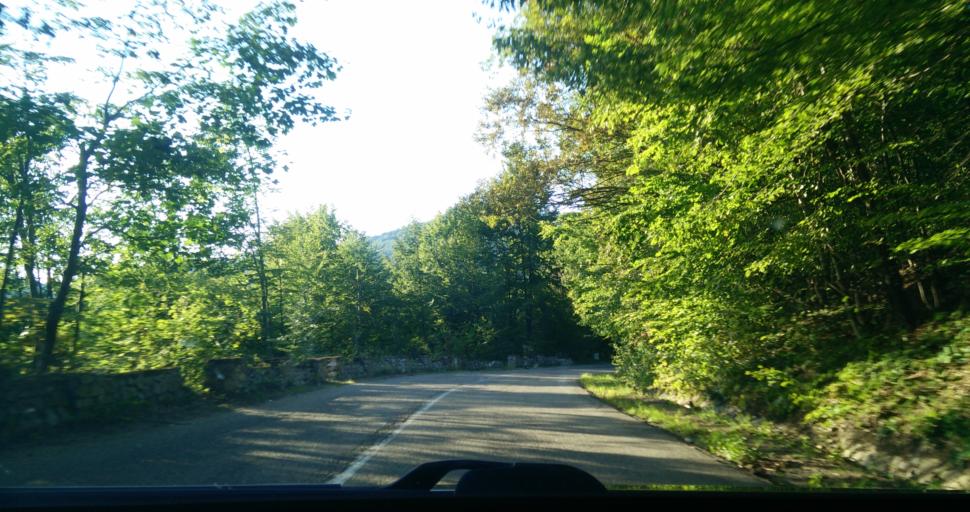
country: RO
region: Bihor
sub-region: Oras Nucet
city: Nucet
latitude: 46.4989
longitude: 22.6081
